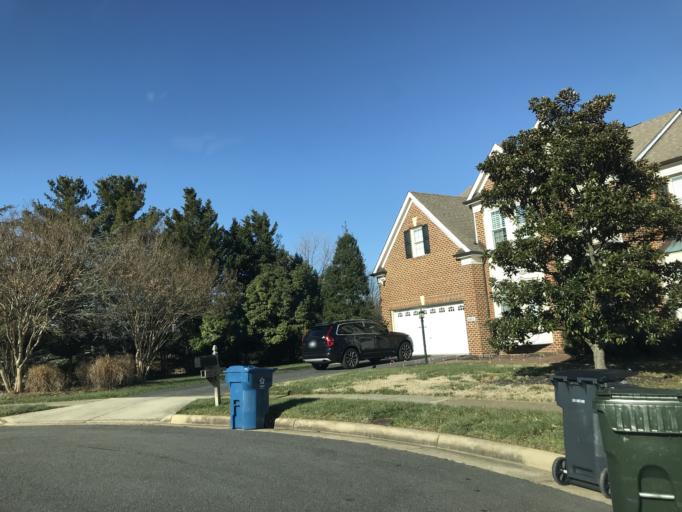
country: US
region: Virginia
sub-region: Fairfax County
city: Franconia
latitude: 38.7824
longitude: -77.1609
